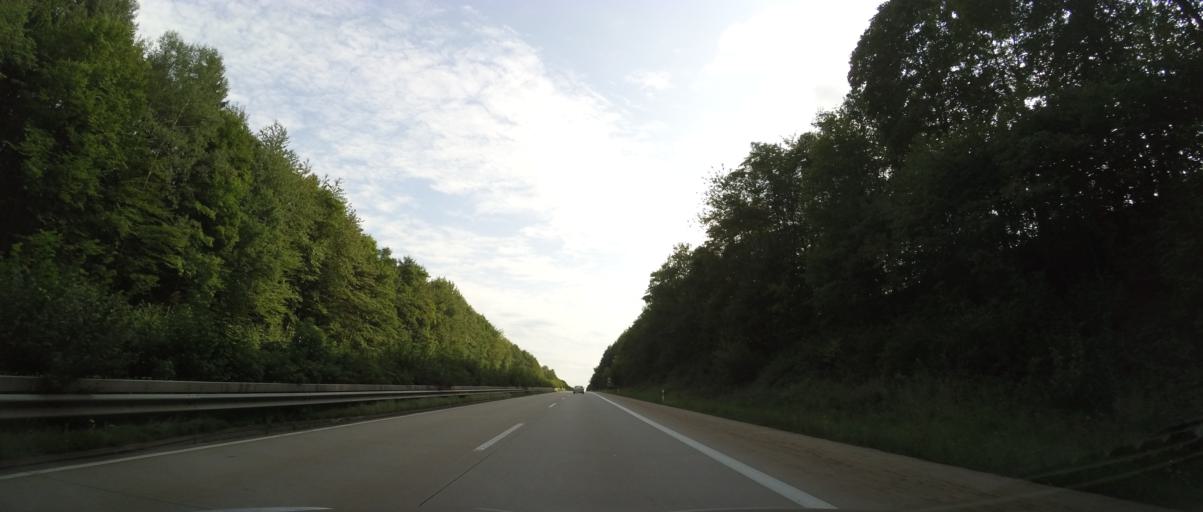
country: DE
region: Rheinland-Pfalz
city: Brockscheid
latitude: 50.1323
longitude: 6.8590
